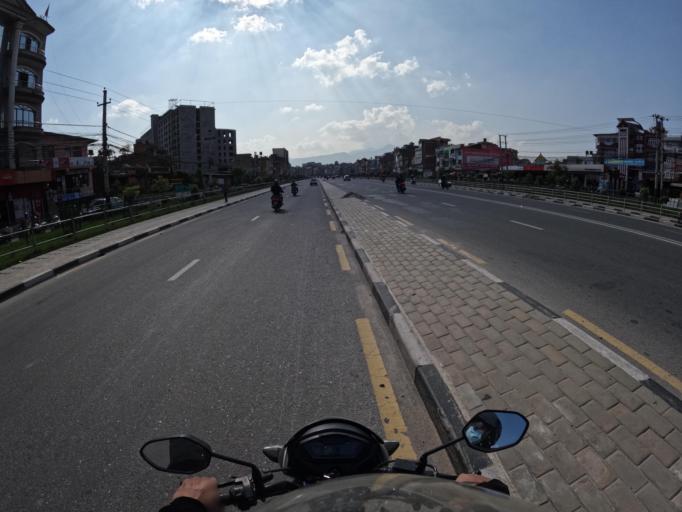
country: NP
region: Central Region
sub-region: Bagmati Zone
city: Patan
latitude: 27.6687
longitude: 85.3355
